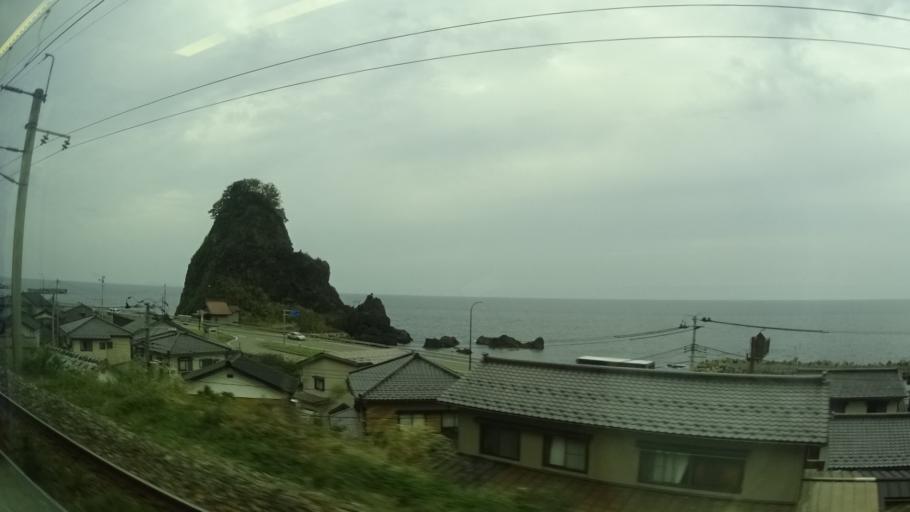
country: JP
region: Yamagata
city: Tsuruoka
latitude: 38.6474
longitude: 139.5980
